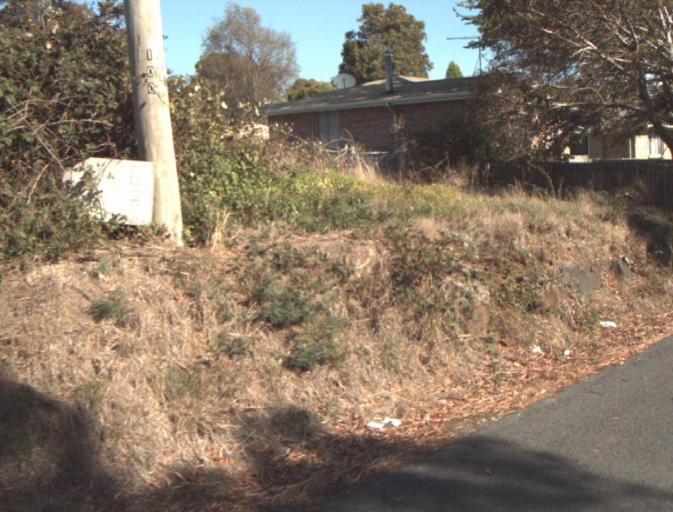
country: AU
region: Tasmania
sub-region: Launceston
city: Mayfield
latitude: -41.3723
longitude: 147.1375
